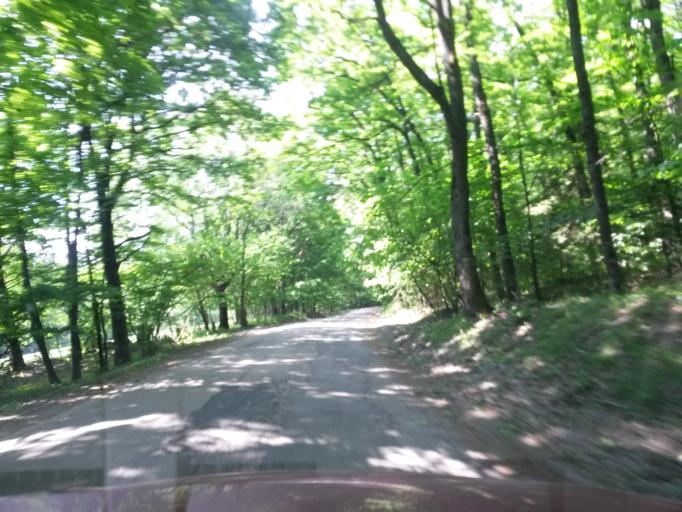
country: SK
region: Kosicky
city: Moldava nad Bodvou
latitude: 48.7154
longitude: 21.0264
